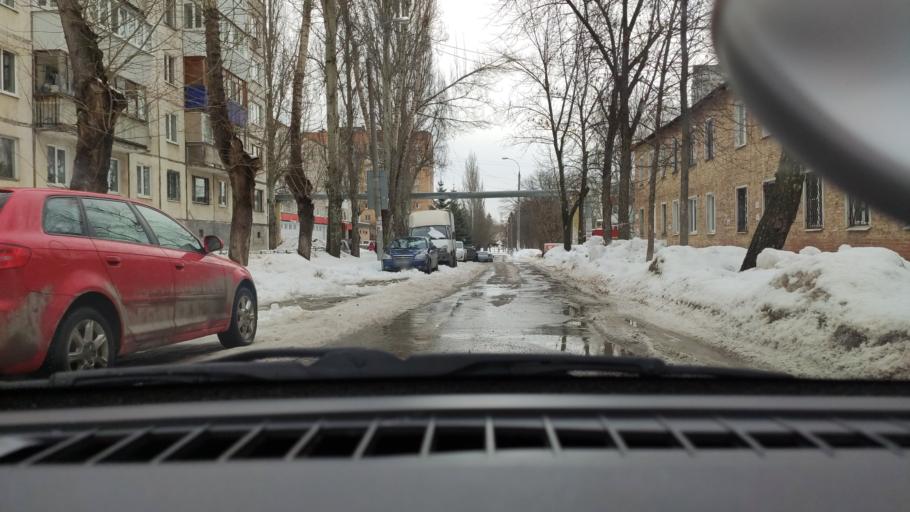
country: RU
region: Samara
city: Petra-Dubrava
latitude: 53.3029
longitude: 50.2729
